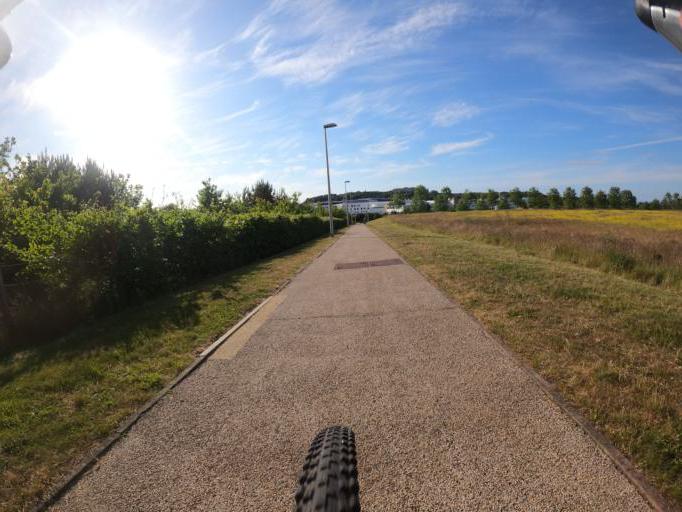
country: GB
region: Scotland
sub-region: Midlothian
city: Loanhead
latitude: 55.9179
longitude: -3.1329
